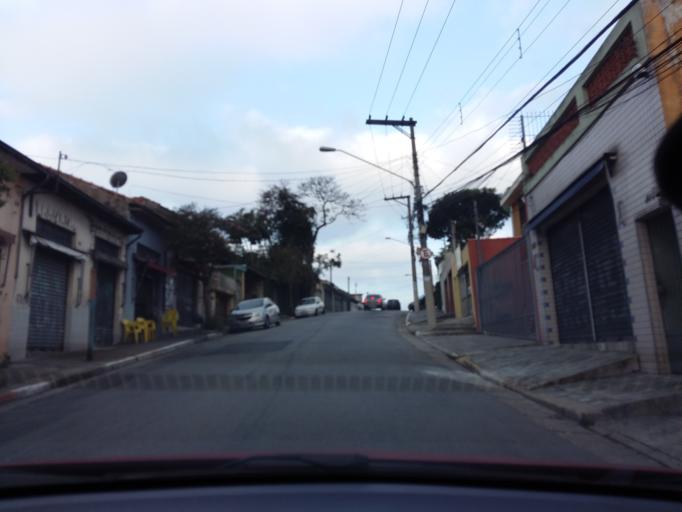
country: BR
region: Sao Paulo
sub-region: Sao Caetano Do Sul
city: Sao Caetano do Sul
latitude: -23.6348
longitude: -46.5908
